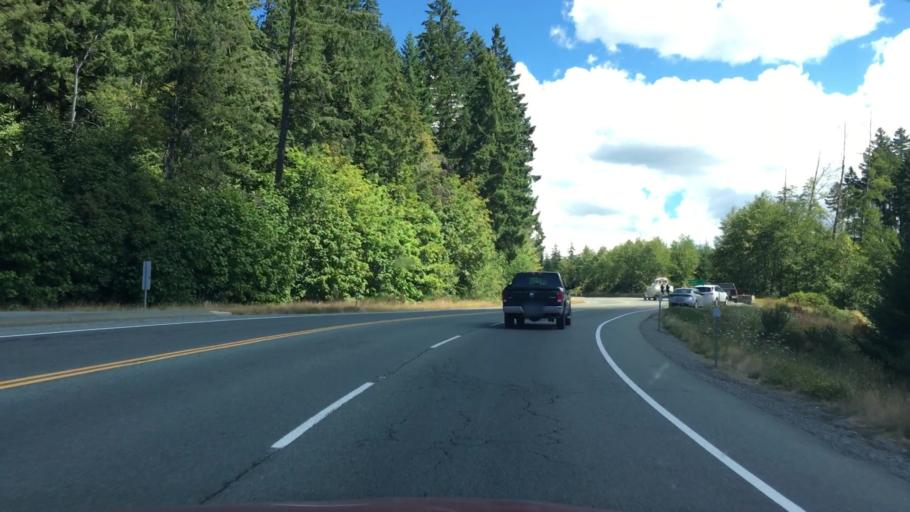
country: CA
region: British Columbia
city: Port Alberni
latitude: 49.2656
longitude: -124.7466
